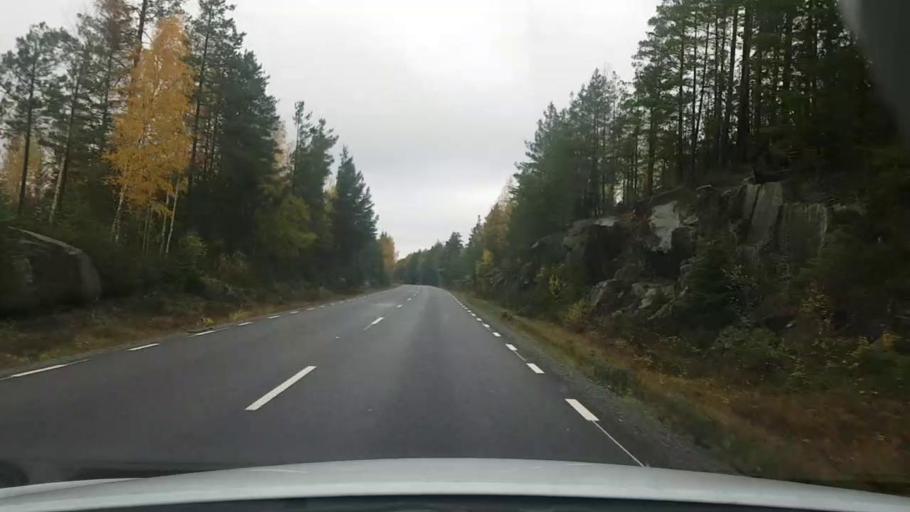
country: SE
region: OErebro
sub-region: Laxa Kommun
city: Laxa
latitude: 58.8465
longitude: 14.5487
